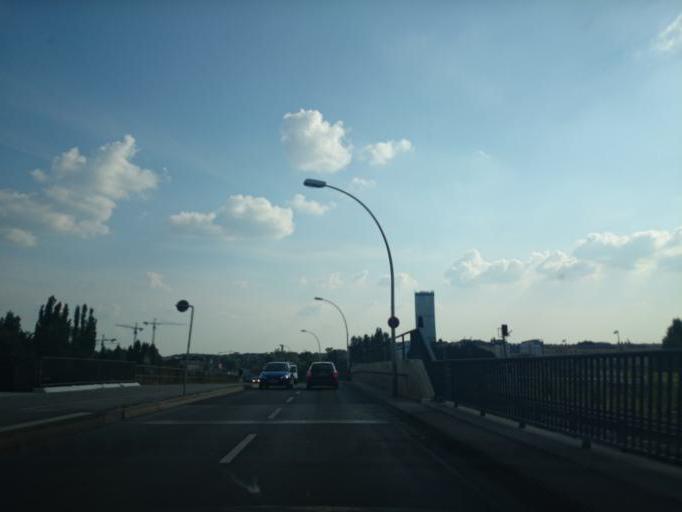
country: DE
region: Berlin
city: Treptow Bezirk
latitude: 52.5025
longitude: 13.4698
